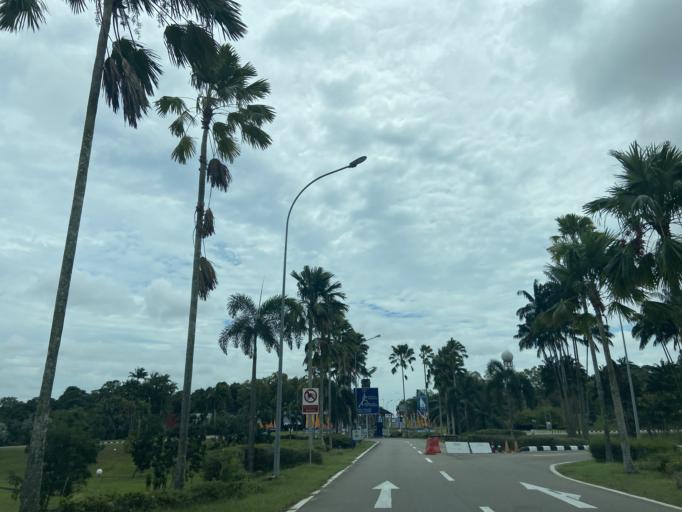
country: SG
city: Singapore
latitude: 1.1224
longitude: 104.1135
